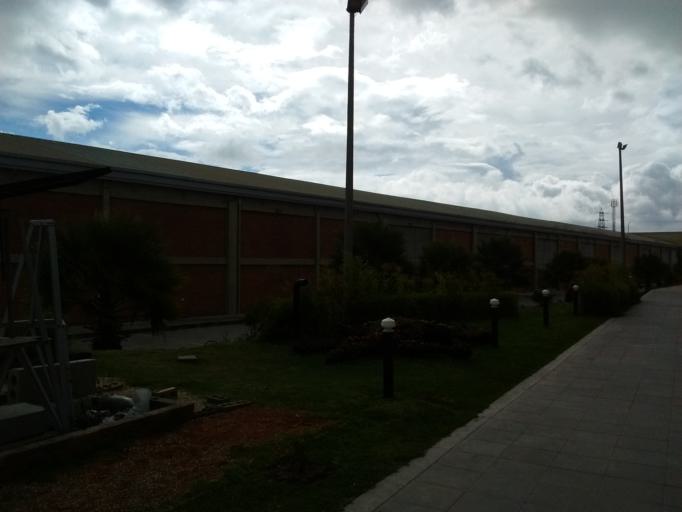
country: CO
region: Cundinamarca
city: Soacha
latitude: 4.5917
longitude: -74.1904
